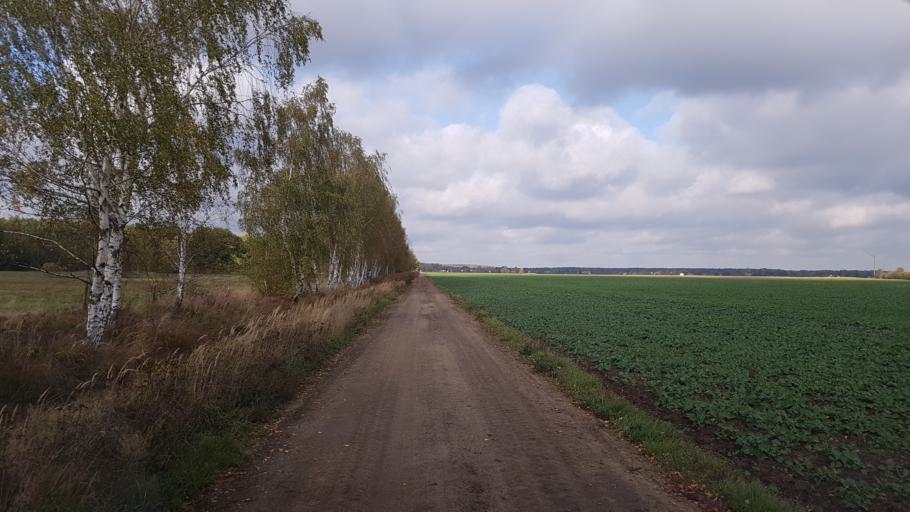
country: DE
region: Brandenburg
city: Schonborn
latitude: 51.5778
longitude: 13.4942
